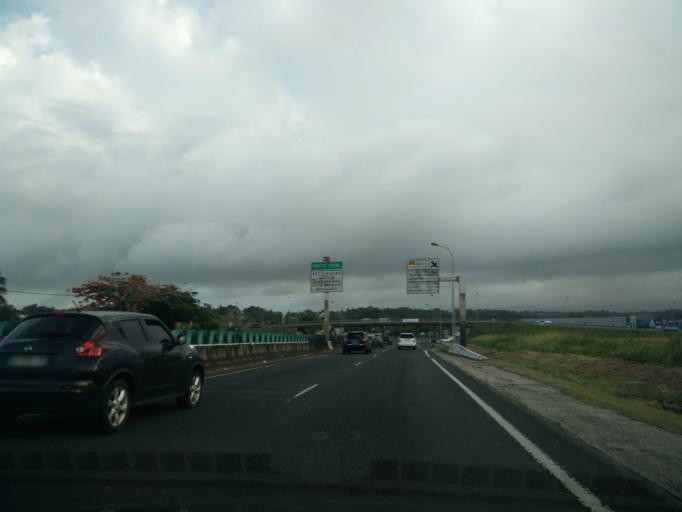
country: GP
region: Guadeloupe
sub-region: Guadeloupe
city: Petit-Bourg
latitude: 16.2038
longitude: -61.6051
